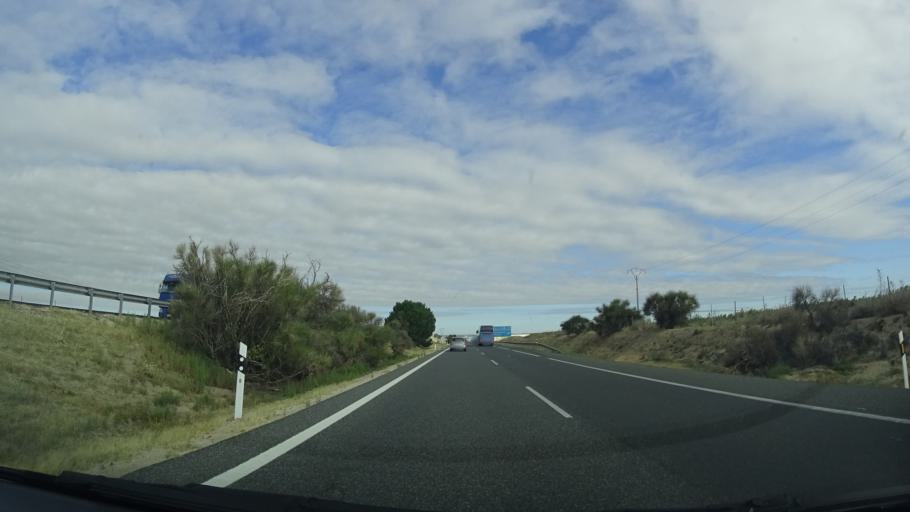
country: ES
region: Castille and Leon
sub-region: Provincia de Valladolid
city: San Vicente del Palacio
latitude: 41.2265
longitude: -4.8485
